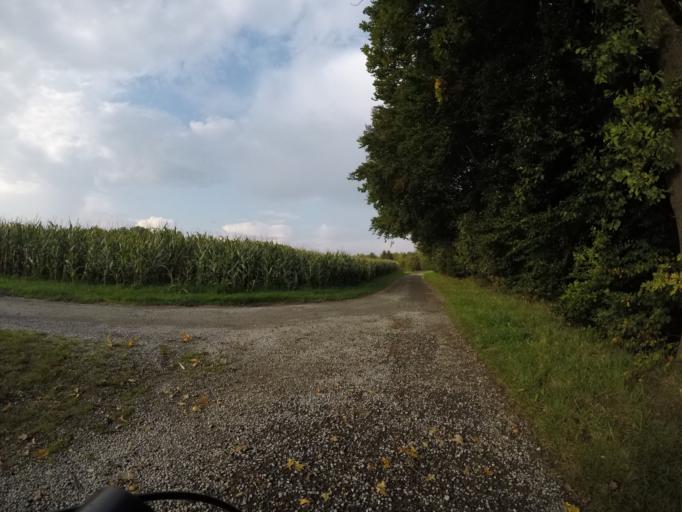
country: DE
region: North Rhine-Westphalia
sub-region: Regierungsbezirk Detmold
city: Herford
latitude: 52.1098
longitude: 8.6440
